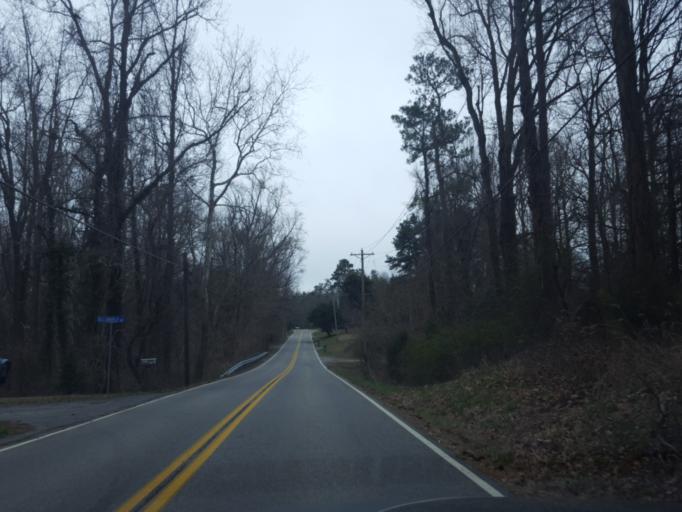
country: US
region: Maryland
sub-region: Calvert County
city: Lusby
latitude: 38.4072
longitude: -76.5027
